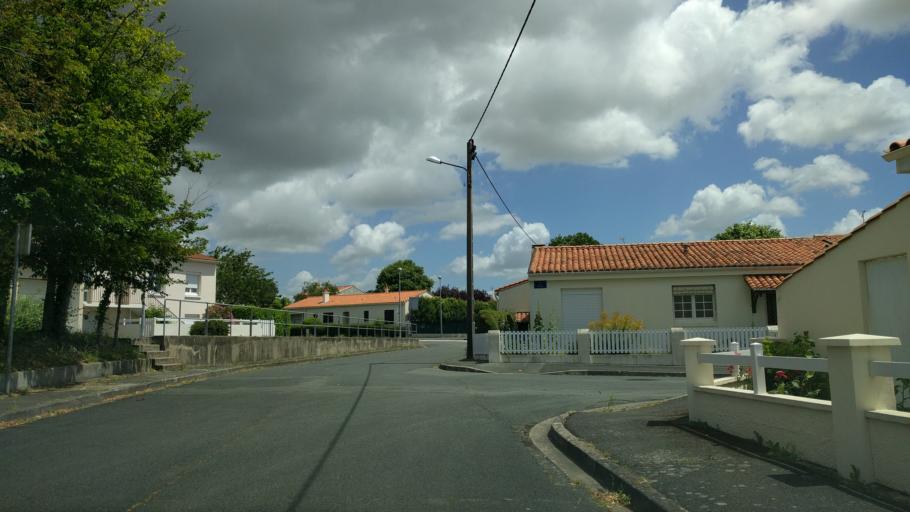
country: FR
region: Poitou-Charentes
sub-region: Departement de la Charente-Maritime
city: La Rochelle
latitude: 46.1667
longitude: -1.1286
